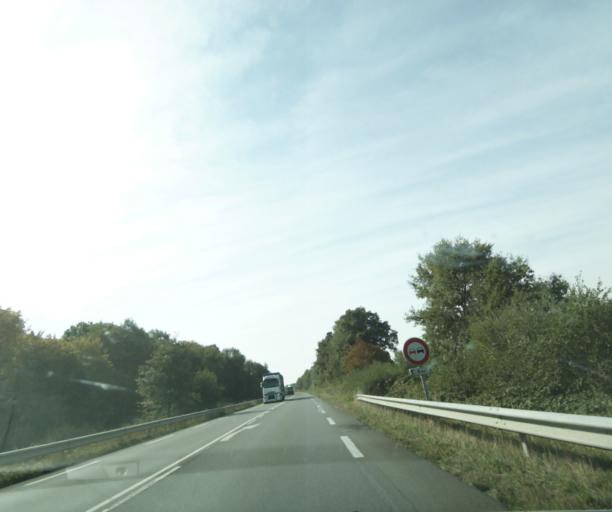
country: FR
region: Bourgogne
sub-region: Departement de Saone-et-Loire
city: Palinges
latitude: 46.5308
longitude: 4.1673
